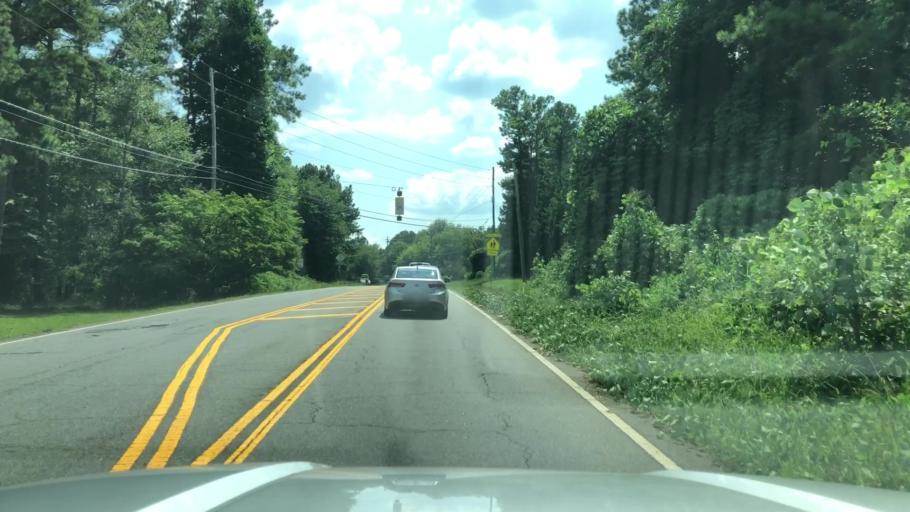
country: US
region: Georgia
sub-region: Cobb County
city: Acworth
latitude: 33.9887
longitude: -84.7128
